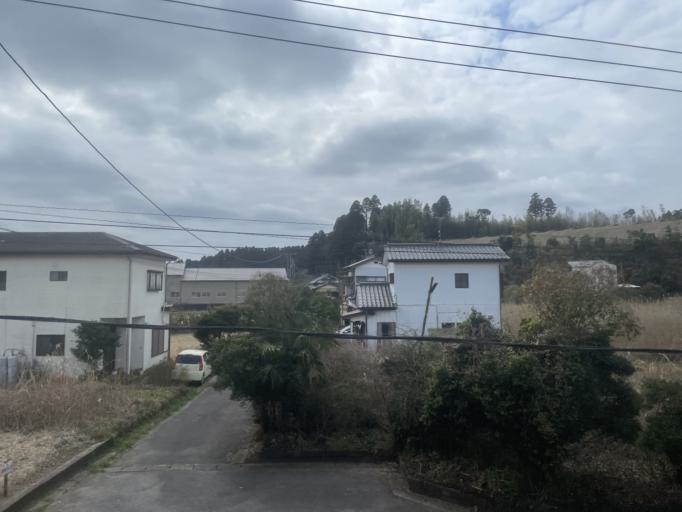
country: JP
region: Chiba
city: Yachimata
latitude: 35.6324
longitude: 140.3562
